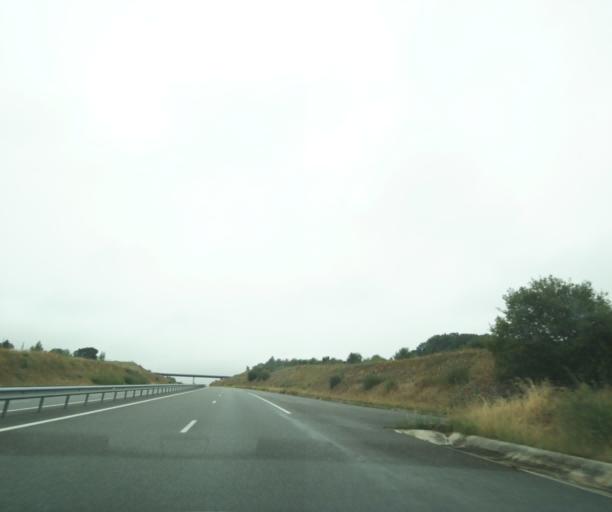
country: FR
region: Midi-Pyrenees
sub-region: Departement du Tarn
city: Carmaux
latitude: 44.0556
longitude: 2.2144
